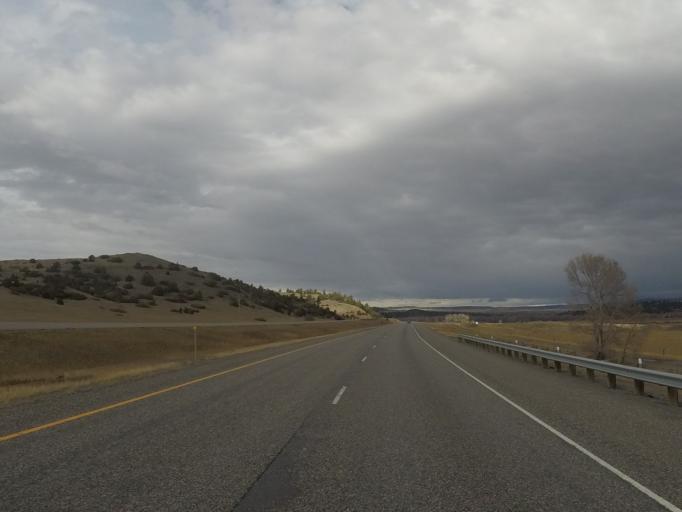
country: US
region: Montana
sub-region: Stillwater County
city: Absarokee
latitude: 45.6930
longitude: -109.4841
